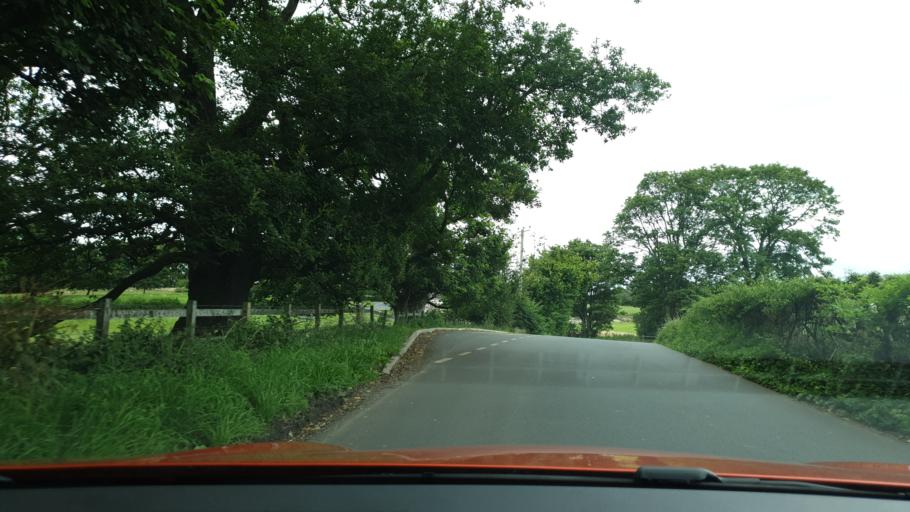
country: GB
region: England
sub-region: Cumbria
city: Penrith
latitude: 54.6123
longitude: -2.8144
